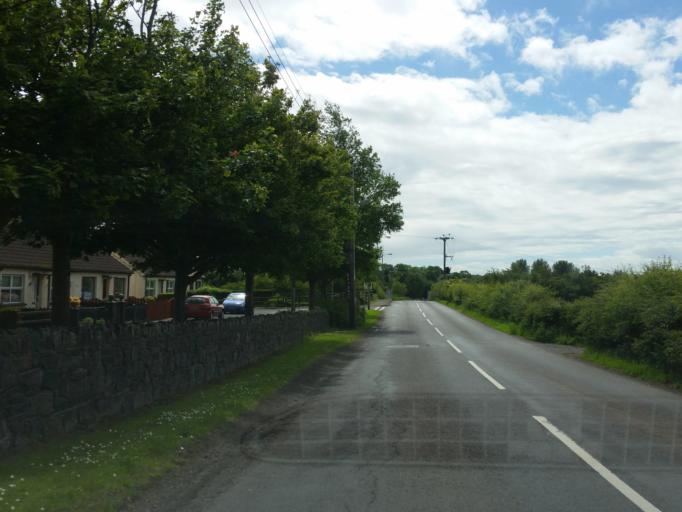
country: GB
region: Northern Ireland
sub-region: Omagh District
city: Omagh
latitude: 54.5537
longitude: -7.1534
